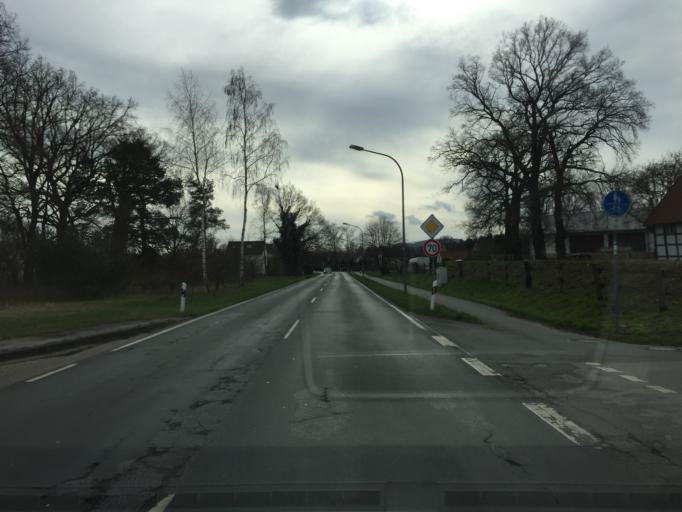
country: DE
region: North Rhine-Westphalia
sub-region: Regierungsbezirk Detmold
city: Lage
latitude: 51.9623
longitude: 8.8054
